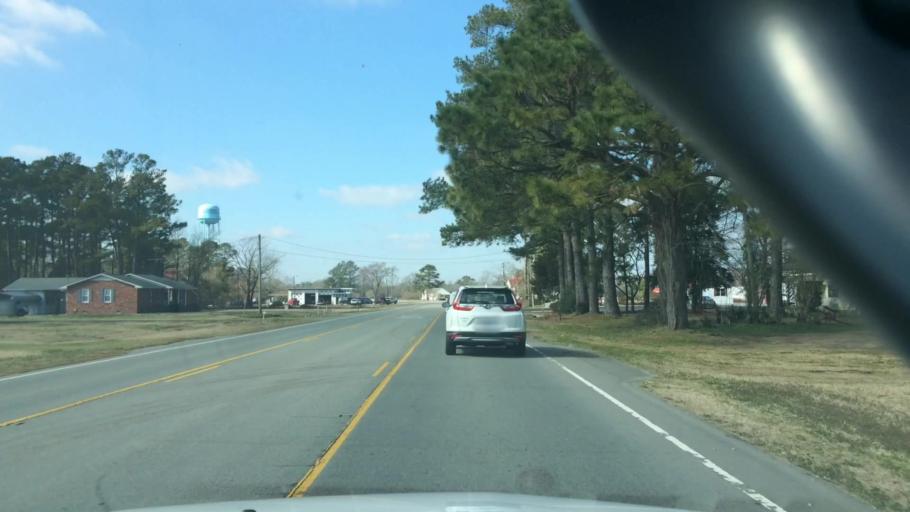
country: US
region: North Carolina
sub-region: Duplin County
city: Beulaville
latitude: 34.8318
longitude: -77.8201
